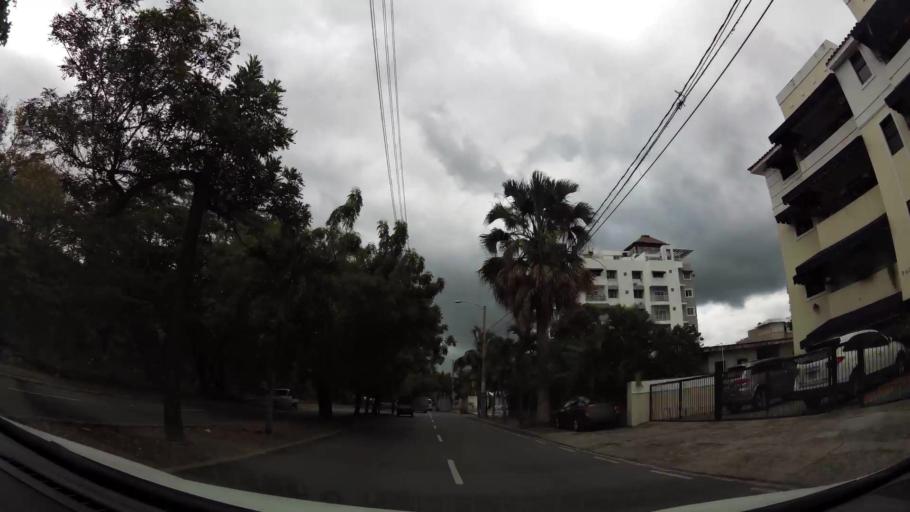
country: DO
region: Nacional
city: Bella Vista
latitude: 18.4494
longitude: -69.9374
